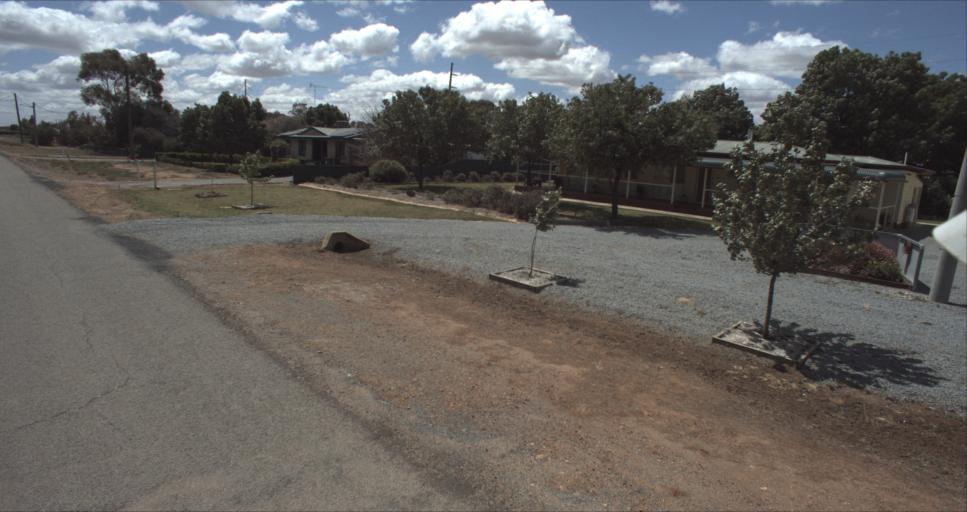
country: AU
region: New South Wales
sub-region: Murrumbidgee Shire
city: Darlington Point
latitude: -34.5116
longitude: 146.1847
